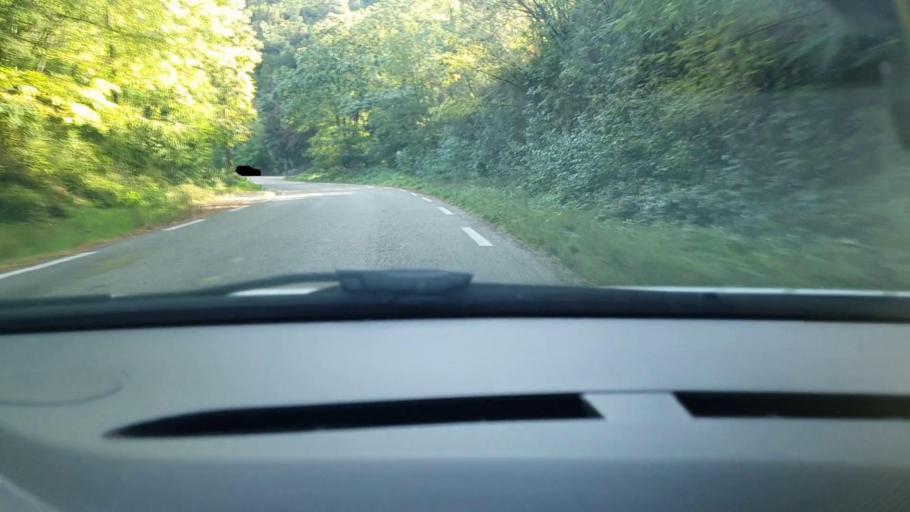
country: FR
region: Languedoc-Roussillon
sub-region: Departement du Gard
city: Besseges
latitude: 44.2882
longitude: 4.0696
